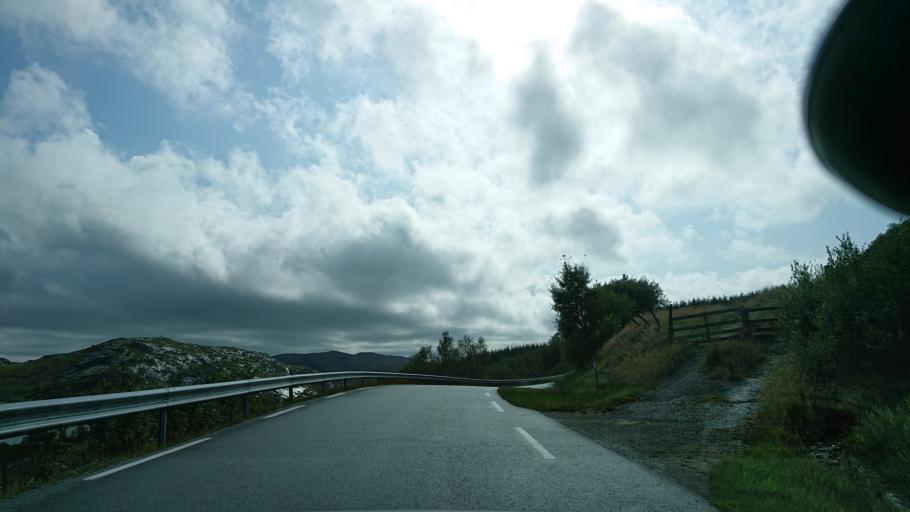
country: NO
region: Rogaland
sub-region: Gjesdal
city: Algard
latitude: 58.6912
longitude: 5.8795
